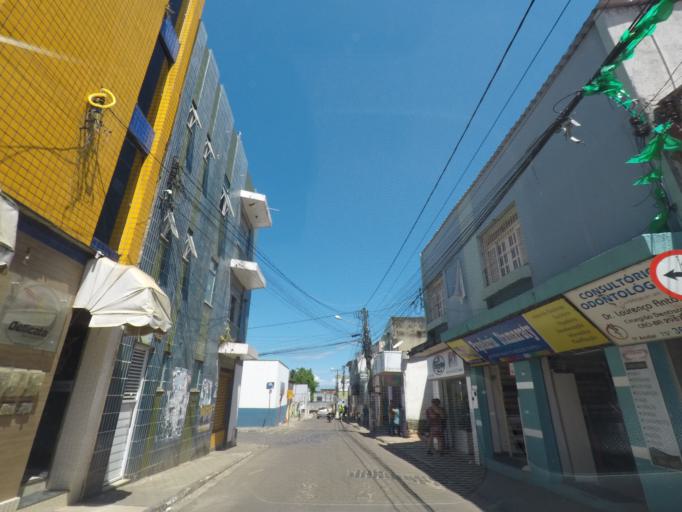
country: BR
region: Bahia
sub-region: Valenca
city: Valenca
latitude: -13.3710
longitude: -39.0719
